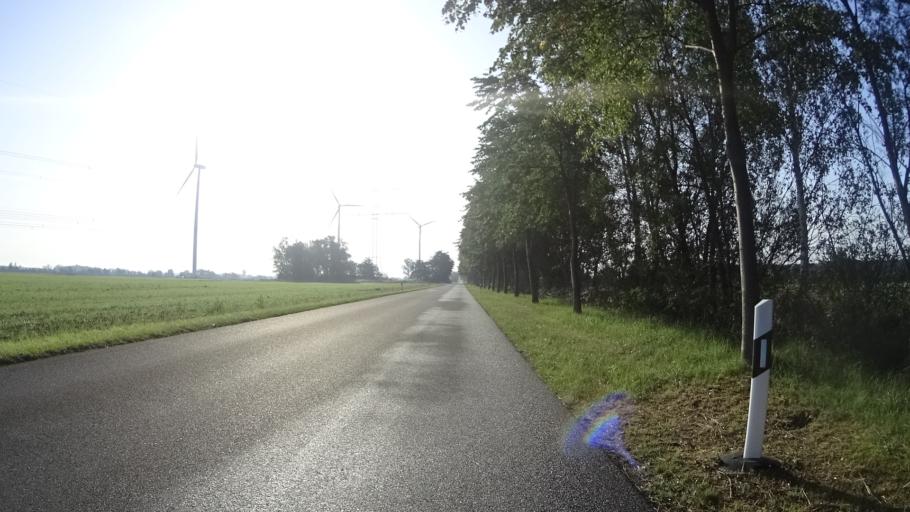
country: DE
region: Brandenburg
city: Kasel-Golzig
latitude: 51.9839
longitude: 13.7216
